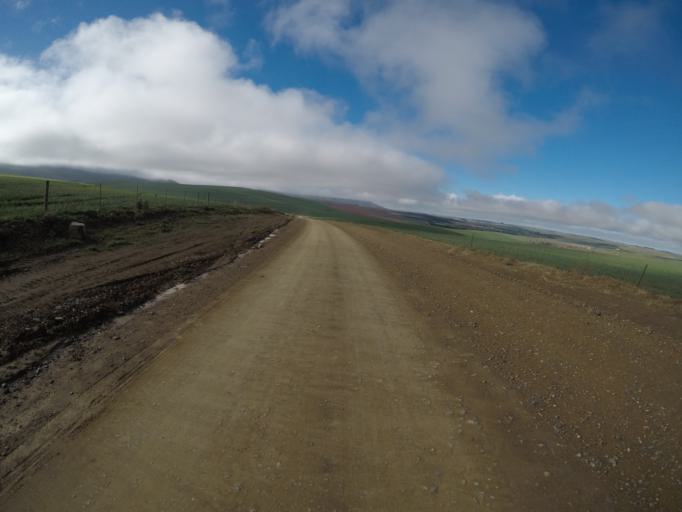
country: ZA
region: Western Cape
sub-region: Overberg District Municipality
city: Caledon
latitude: -34.1096
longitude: 19.7610
